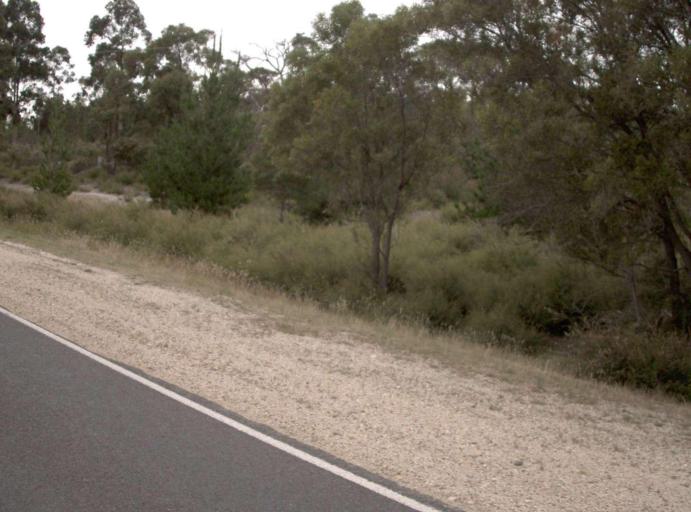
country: AU
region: Victoria
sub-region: Wellington
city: Sale
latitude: -38.1817
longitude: 147.1414
